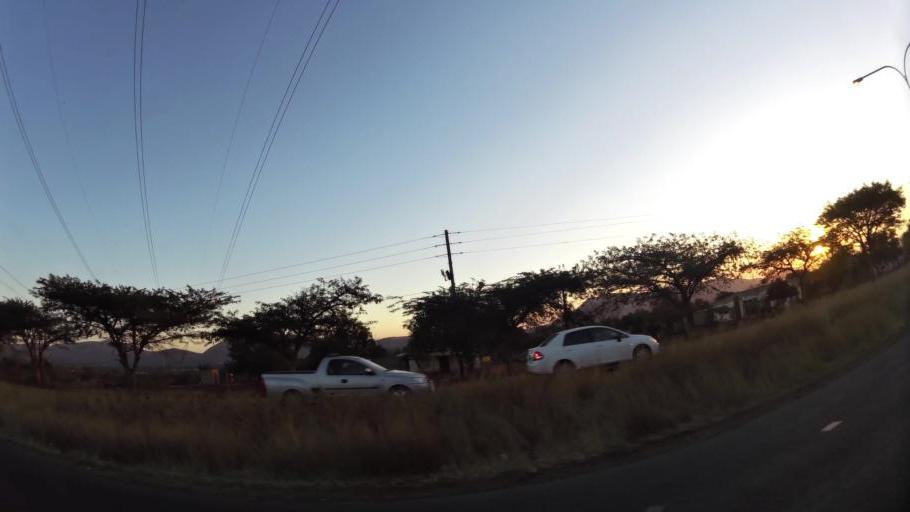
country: ZA
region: North-West
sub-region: Bojanala Platinum District Municipality
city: Rustenburg
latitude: -25.6120
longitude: 27.1775
